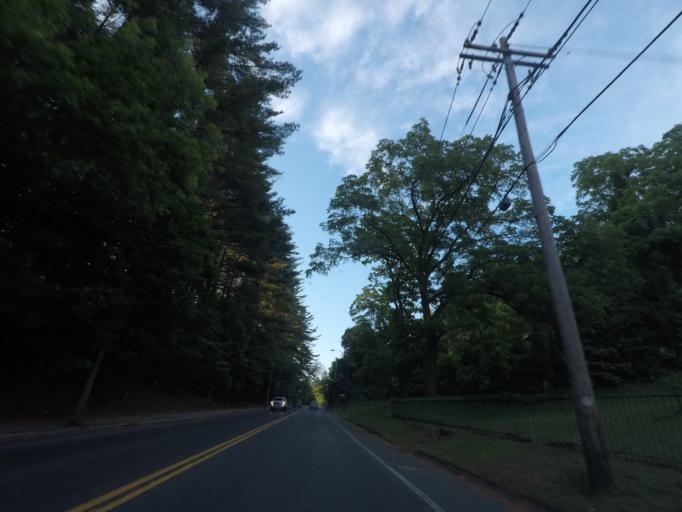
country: US
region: Massachusetts
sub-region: Hampden County
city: Palmer
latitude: 42.1637
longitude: -72.3272
